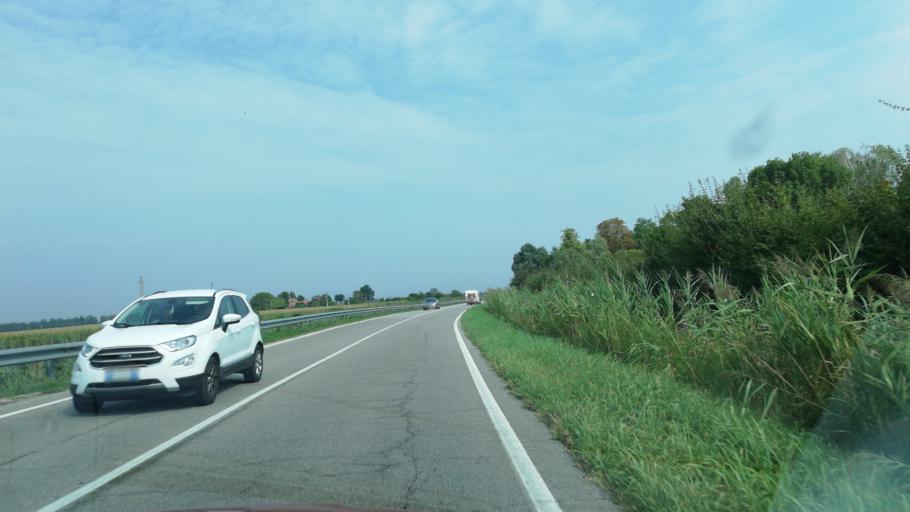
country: IT
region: Veneto
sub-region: Provincia di Venezia
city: La Salute di Livenza
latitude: 45.5978
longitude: 12.8055
